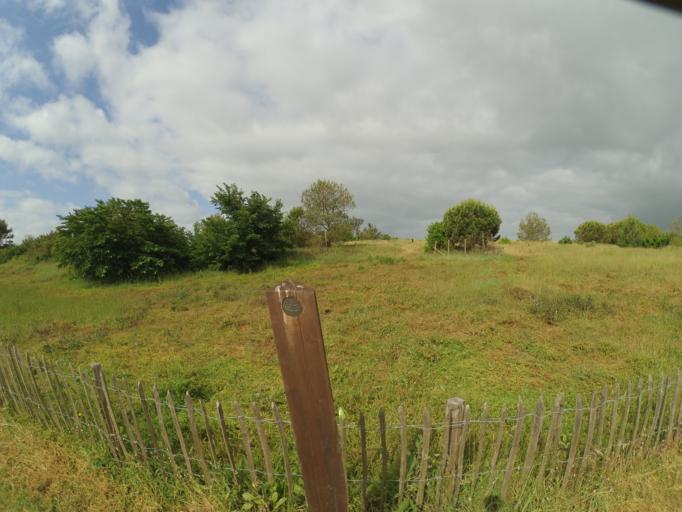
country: FR
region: Poitou-Charentes
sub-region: Departement de la Charente-Maritime
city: Aytre
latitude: 46.1201
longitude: -1.1236
